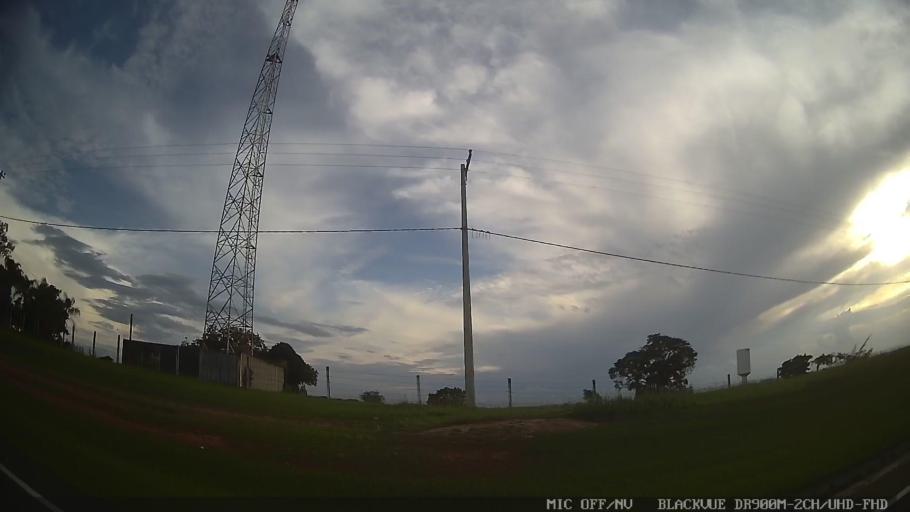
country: BR
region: Sao Paulo
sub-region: Porto Feliz
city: Porto Feliz
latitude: -23.1973
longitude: -47.6156
